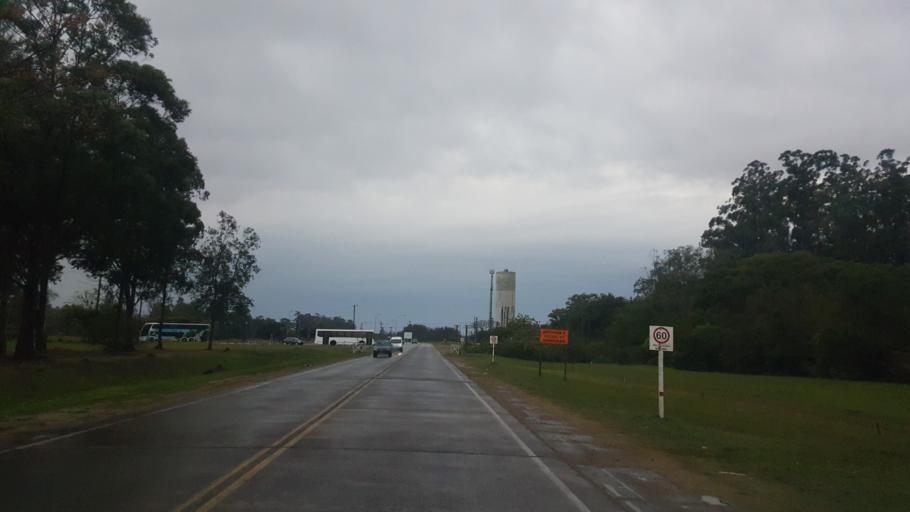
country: AR
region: Corrientes
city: Ituzaingo
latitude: -27.5802
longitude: -56.6749
